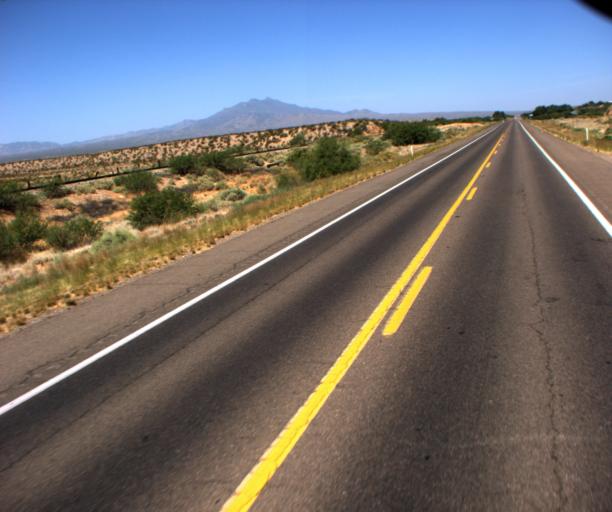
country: US
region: Arizona
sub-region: Graham County
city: Bylas
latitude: 33.0734
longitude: -110.0236
